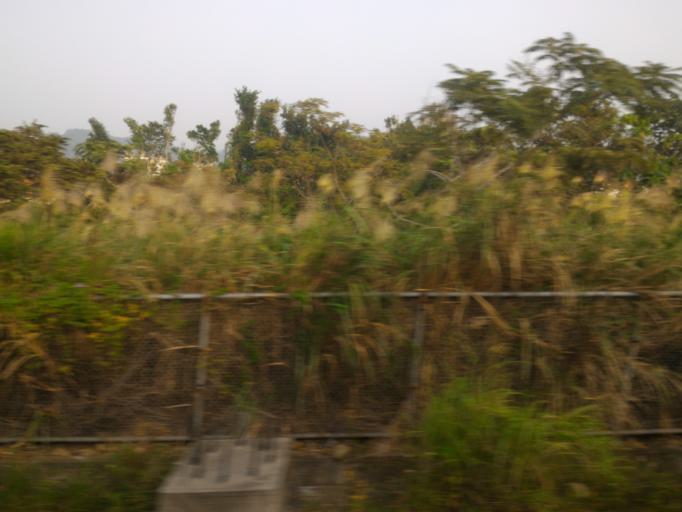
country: TW
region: Taiwan
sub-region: Taoyuan
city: Taoyuan
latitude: 24.9648
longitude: 121.3378
